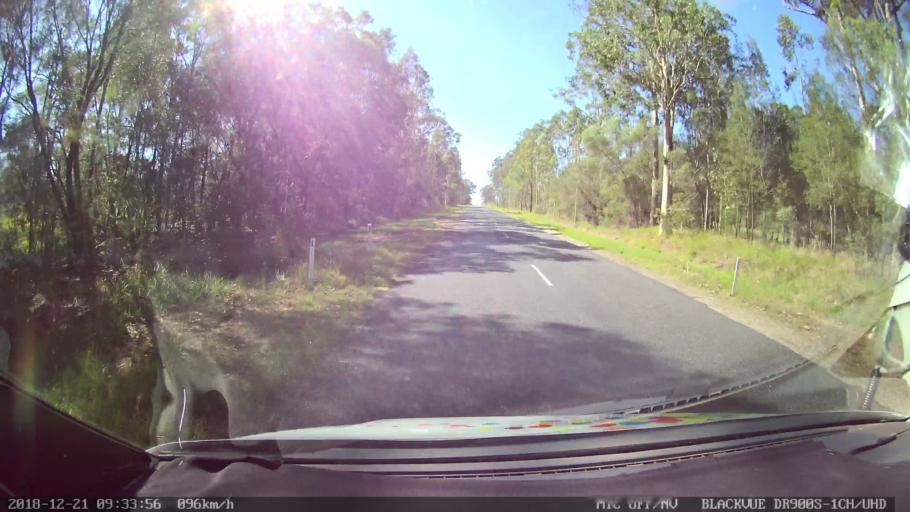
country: AU
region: New South Wales
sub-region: Clarence Valley
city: Grafton
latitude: -29.4914
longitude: 152.9779
